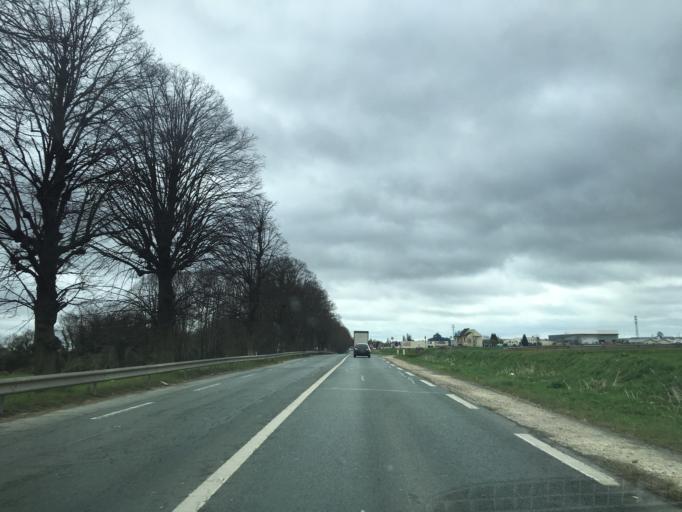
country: FR
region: Ile-de-France
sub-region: Departement du Val-de-Marne
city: Santeny
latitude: 48.7234
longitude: 2.5601
